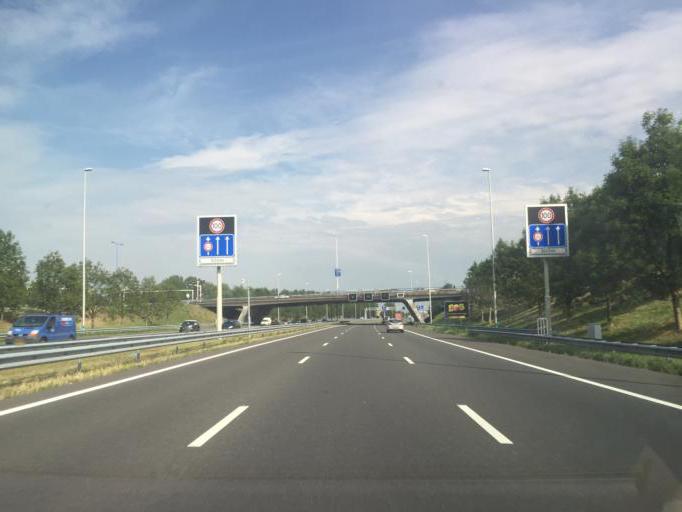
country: NL
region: South Holland
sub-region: Gemeente Zoetermeer
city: Zoetermeer
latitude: 52.0449
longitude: 4.5066
